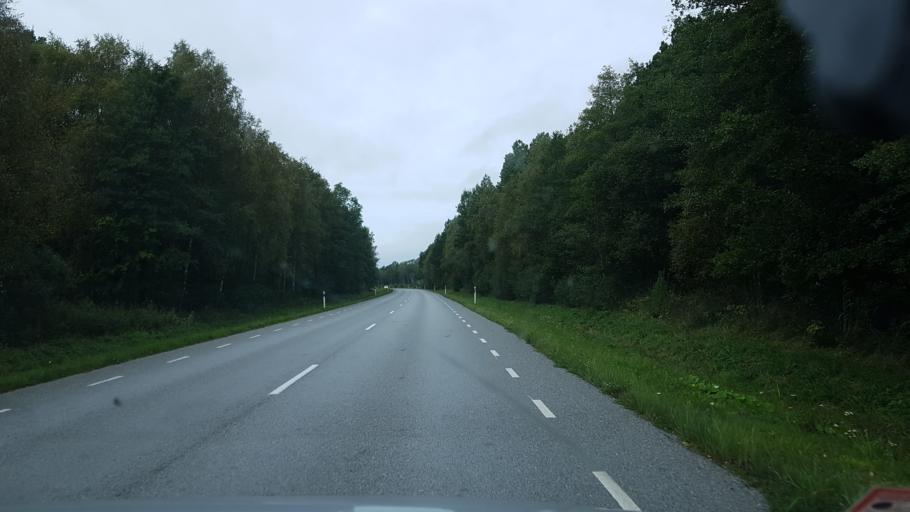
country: EE
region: Hiiumaa
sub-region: Kaerdla linn
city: Kardla
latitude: 59.0039
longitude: 22.5629
